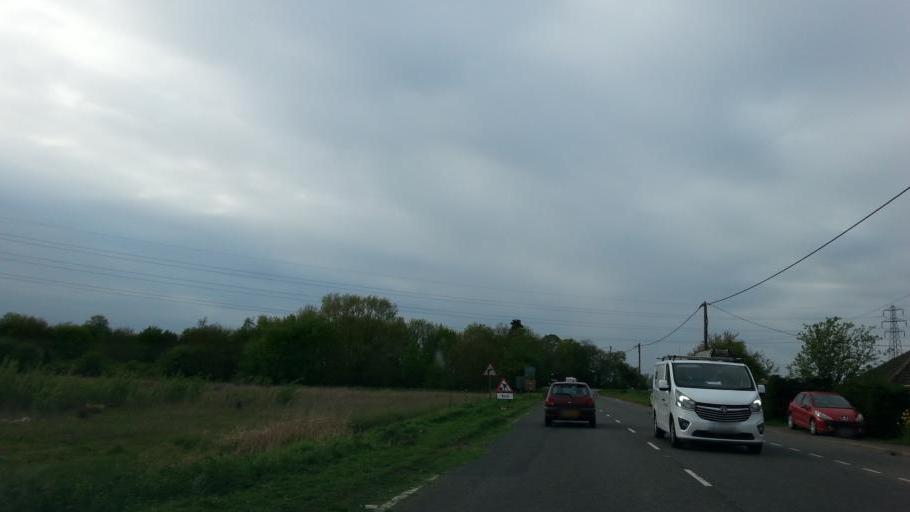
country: GB
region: England
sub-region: Cambridgeshire
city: March
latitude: 52.5731
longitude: 0.0577
